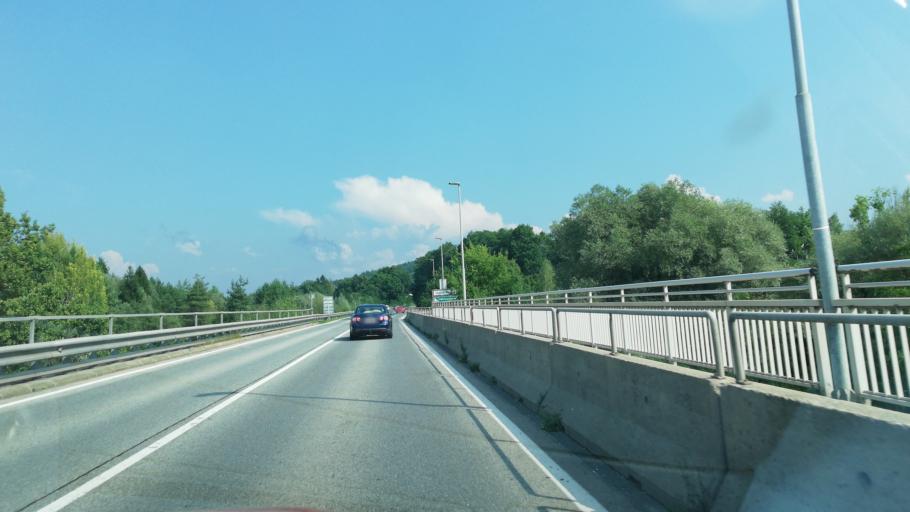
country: AT
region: Carinthia
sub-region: Villach Stadt
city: Villach
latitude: 46.6033
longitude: 13.8759
